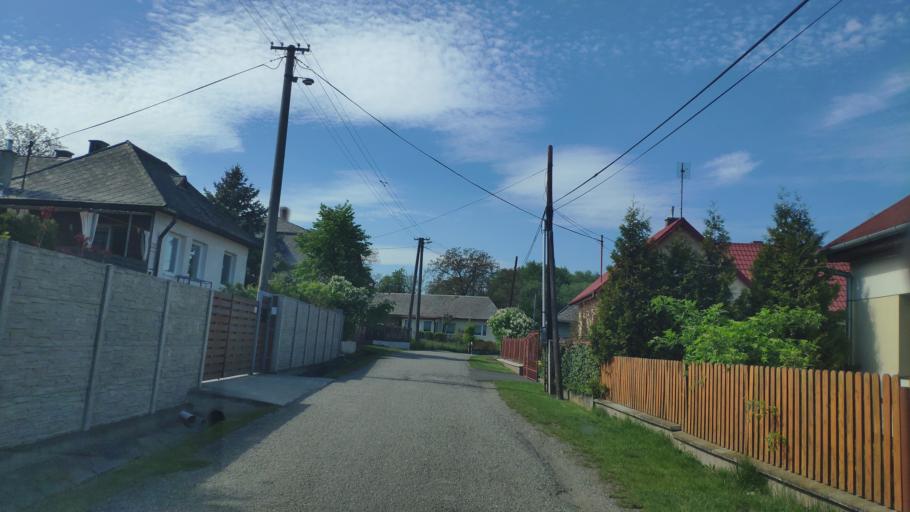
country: SK
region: Kosicky
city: Secovce
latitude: 48.7052
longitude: 21.6162
